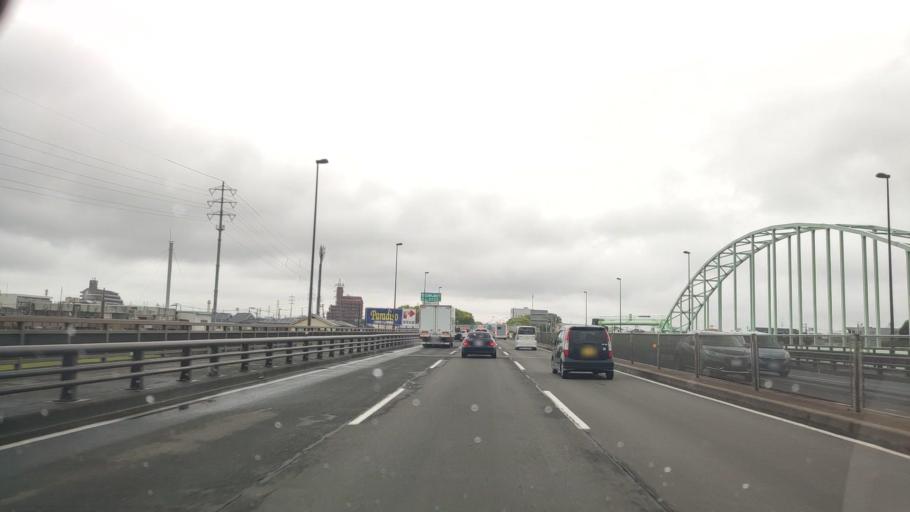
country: JP
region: Miyagi
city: Sendai
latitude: 38.2257
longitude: 140.9015
